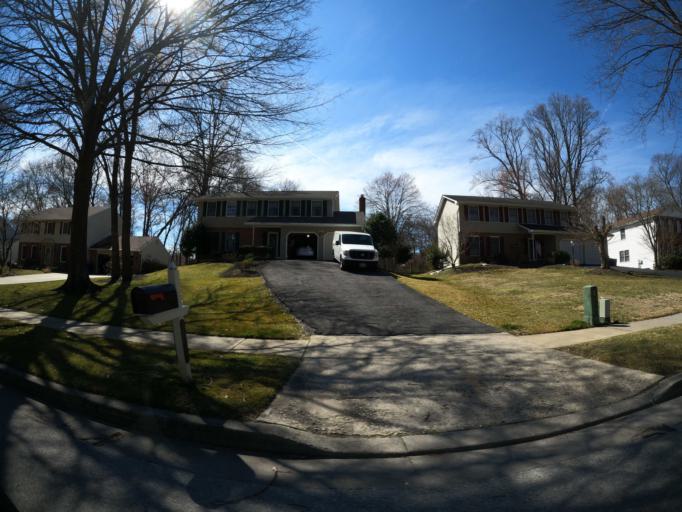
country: US
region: Maryland
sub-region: Howard County
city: Columbia
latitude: 39.2208
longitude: -76.8267
